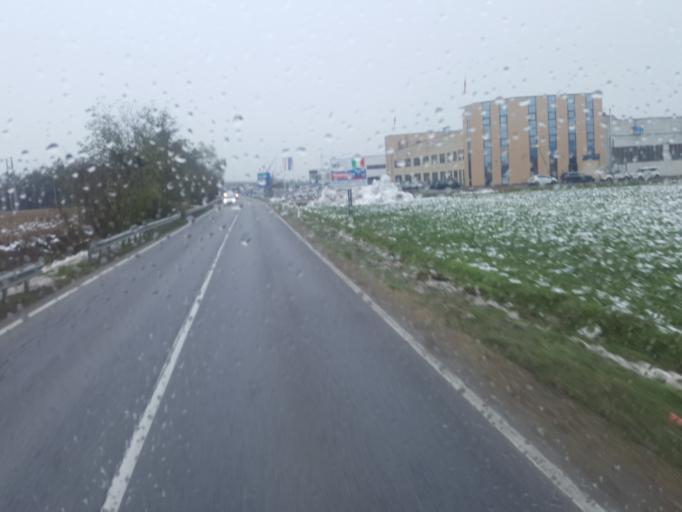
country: IT
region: Piedmont
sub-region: Provincia di Cuneo
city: Breo
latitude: 44.4160
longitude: 7.8442
